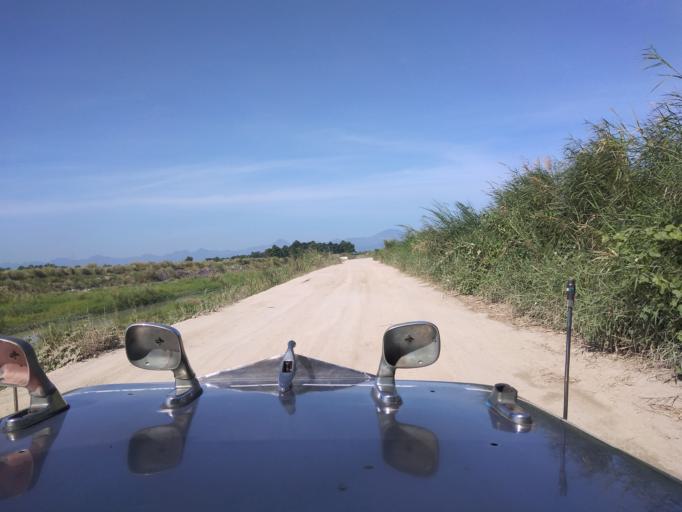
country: PH
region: Central Luzon
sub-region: Province of Pampanga
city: Minalin
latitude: 14.9910
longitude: 120.6757
